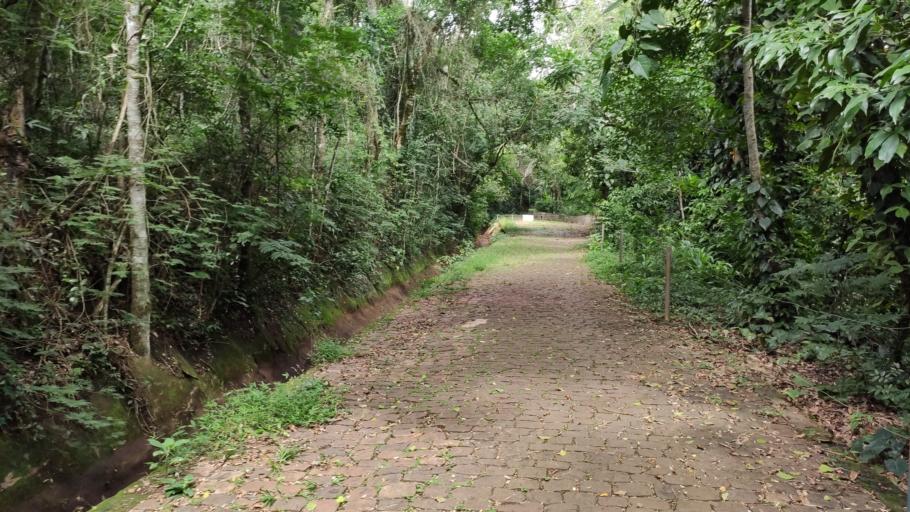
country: BR
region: Parana
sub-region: Londrina
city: Londrina
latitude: -23.3458
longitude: -51.1395
